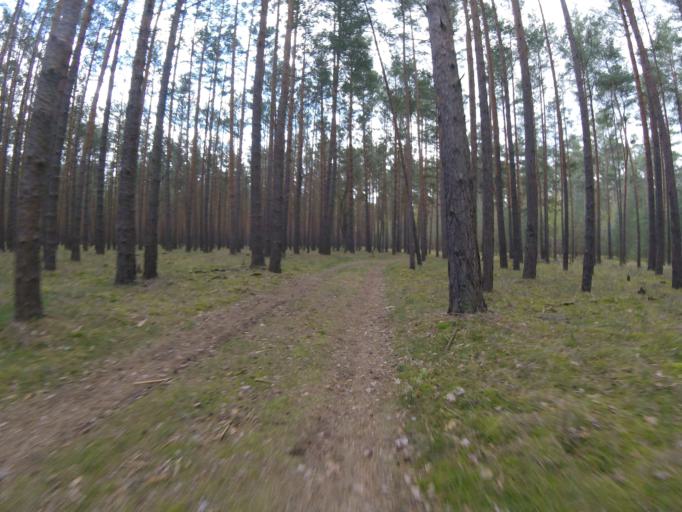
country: DE
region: Brandenburg
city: Bestensee
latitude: 52.2632
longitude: 13.6733
